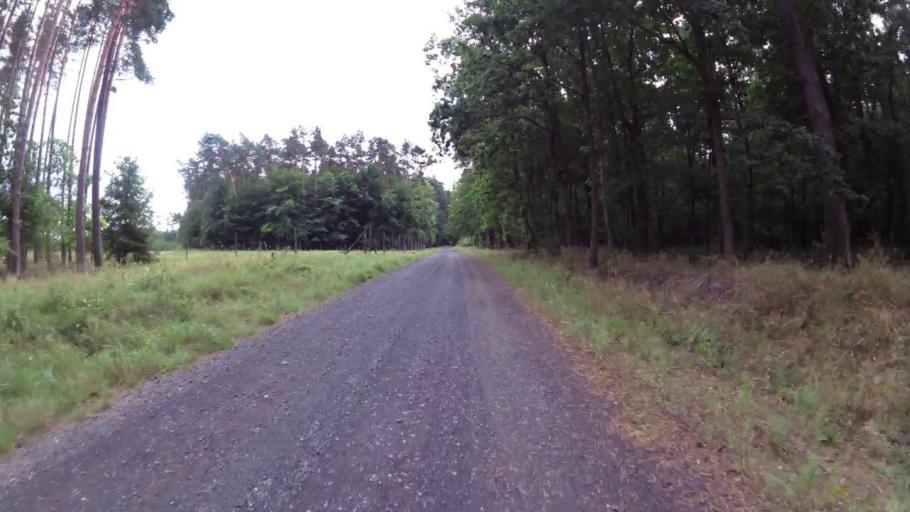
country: PL
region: West Pomeranian Voivodeship
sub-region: Powiat mysliborski
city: Debno
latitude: 52.7707
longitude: 14.7158
